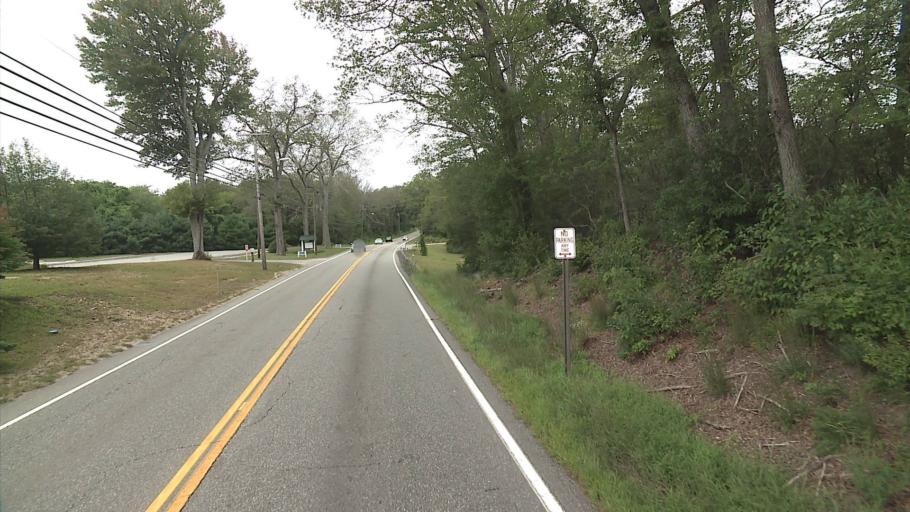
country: US
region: Connecticut
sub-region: New London County
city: Oxoboxo River
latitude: 41.4041
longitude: -72.1810
